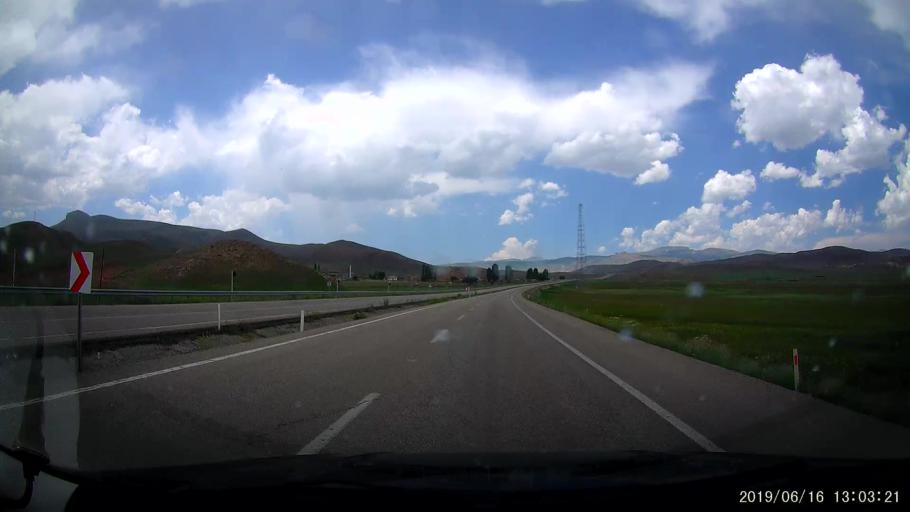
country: TR
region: Agri
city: Sulucem
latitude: 39.5807
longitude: 43.7922
